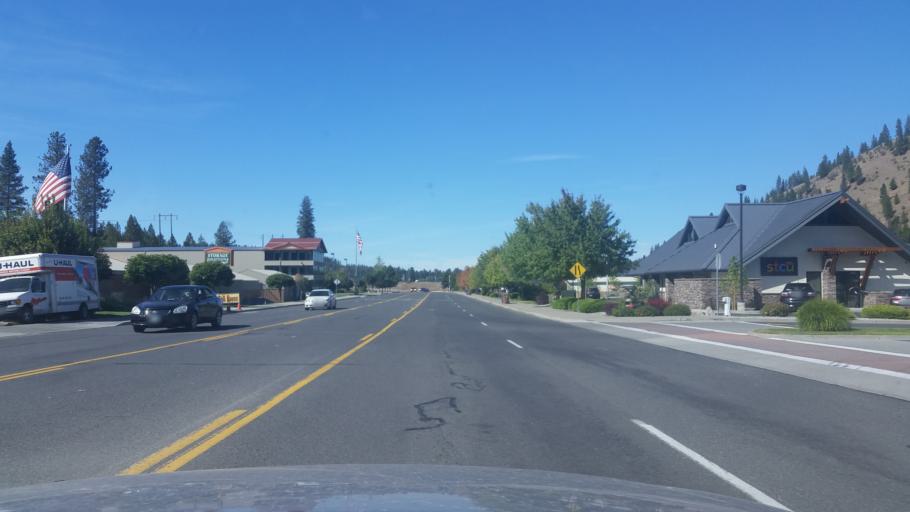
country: US
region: Washington
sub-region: Spokane County
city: Spokane
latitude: 47.6148
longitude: -117.4304
